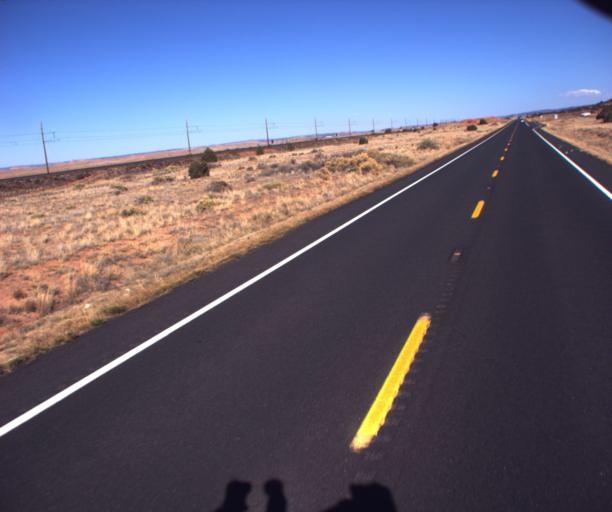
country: US
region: Arizona
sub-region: Coconino County
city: Kaibito
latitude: 36.4158
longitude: -110.8138
